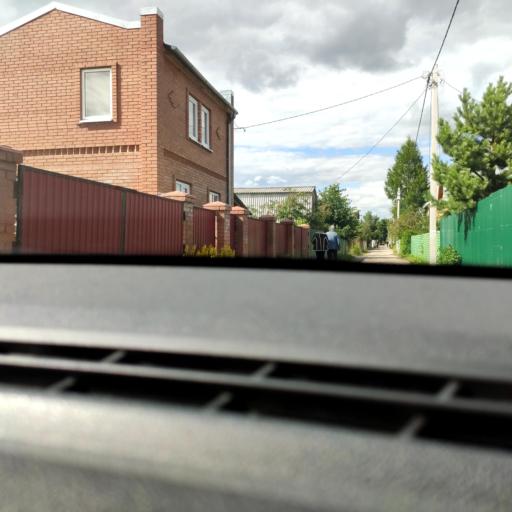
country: RU
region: Samara
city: Podstepki
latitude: 53.5817
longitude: 49.0737
